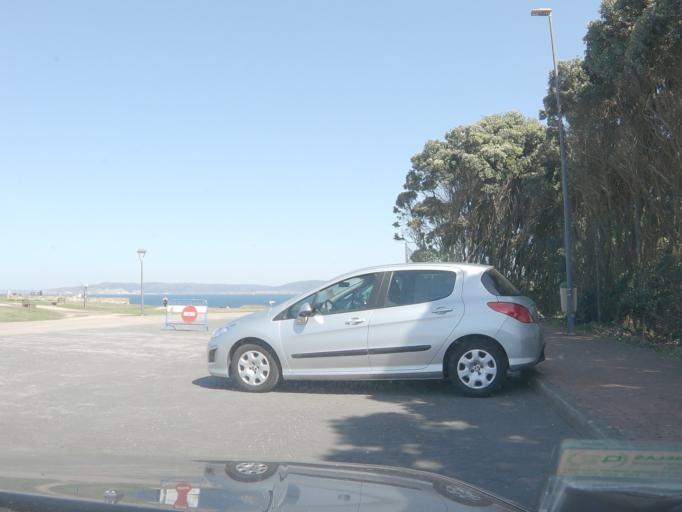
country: ES
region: Galicia
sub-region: Provincia da Coruna
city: A Coruna
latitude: 43.3862
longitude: -8.3986
